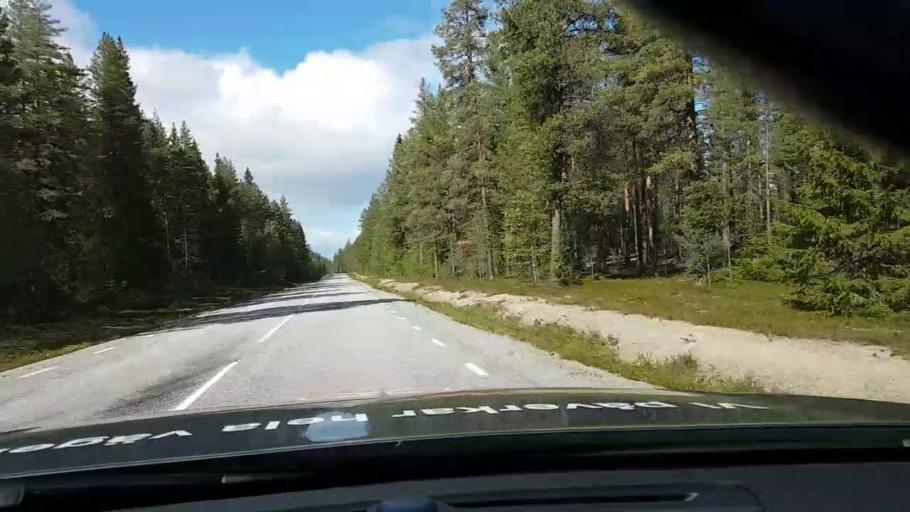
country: SE
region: Vaesternorrland
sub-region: OErnskoeldsviks Kommun
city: Bredbyn
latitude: 63.6637
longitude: 17.8374
